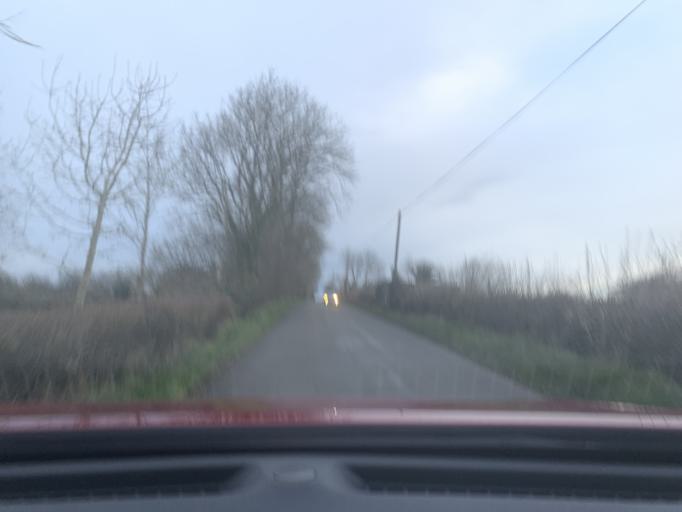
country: IE
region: Connaught
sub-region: Roscommon
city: Ballaghaderreen
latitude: 53.8741
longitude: -8.5589
